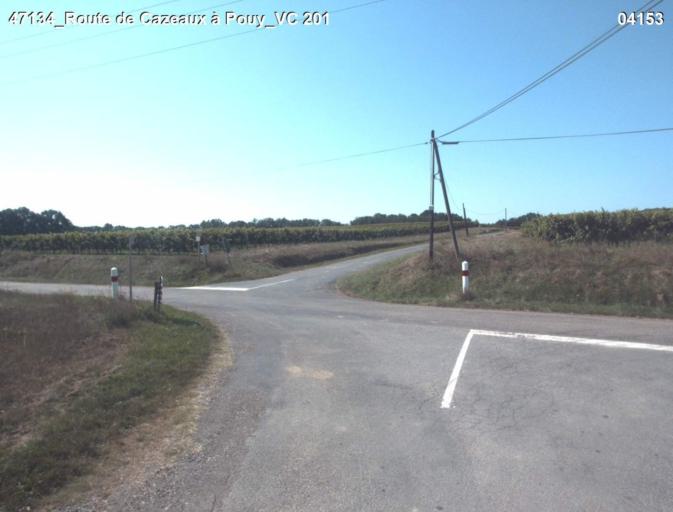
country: FR
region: Aquitaine
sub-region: Departement du Lot-et-Garonne
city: Mezin
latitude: 44.0333
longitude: 0.3114
